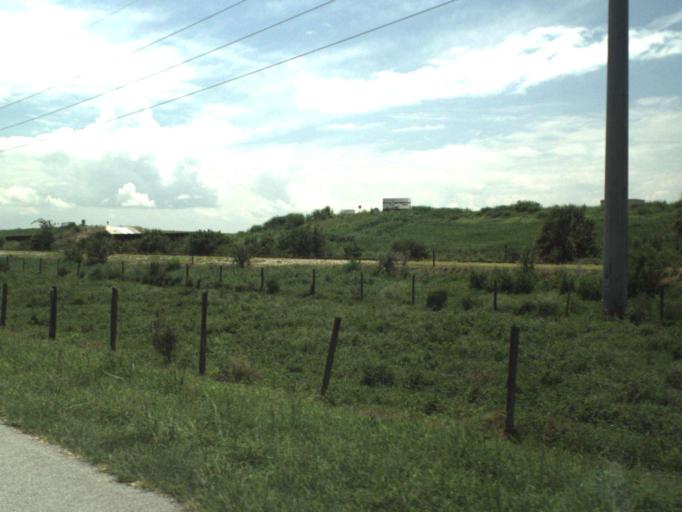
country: US
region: Florida
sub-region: Palm Beach County
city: Pahokee
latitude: 26.9020
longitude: -80.6111
